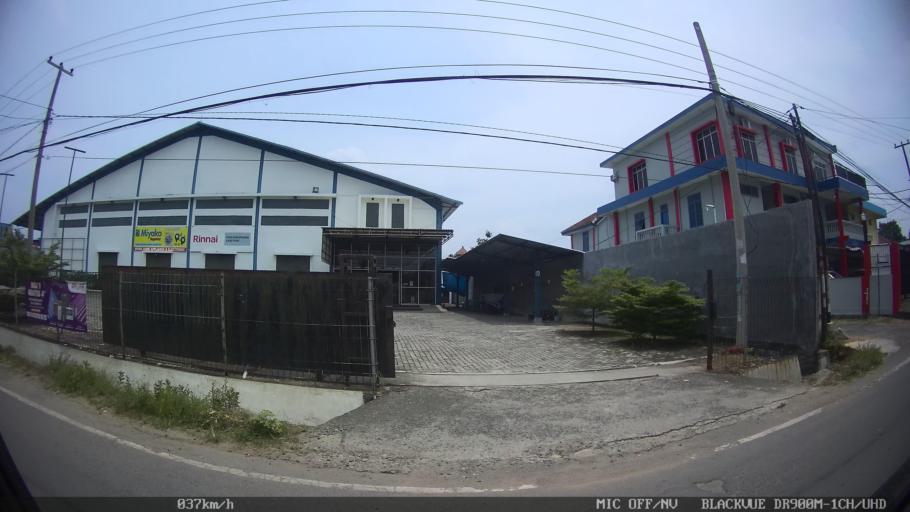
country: ID
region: Lampung
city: Bandarlampung
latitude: -5.4105
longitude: 105.2889
